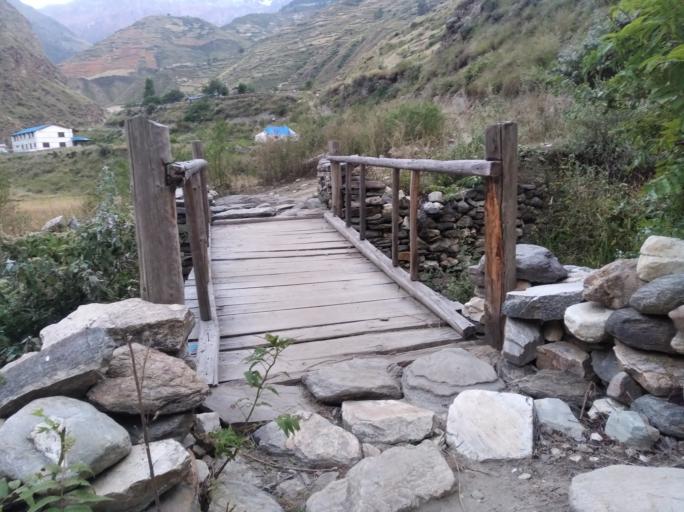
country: NP
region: Western Region
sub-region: Dhawalagiri Zone
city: Jomsom
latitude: 28.8904
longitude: 82.9840
